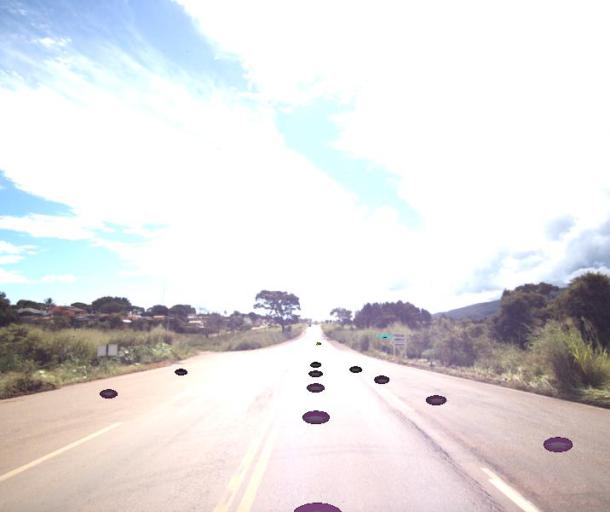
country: BR
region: Goias
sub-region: Pirenopolis
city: Pirenopolis
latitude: -16.0193
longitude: -49.1101
